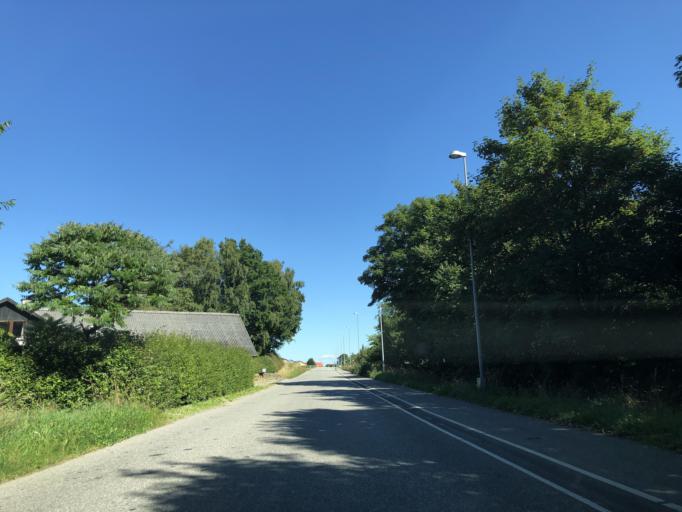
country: DK
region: North Denmark
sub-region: Mariagerfjord Kommune
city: Hobro
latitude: 56.6416
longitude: 9.7759
